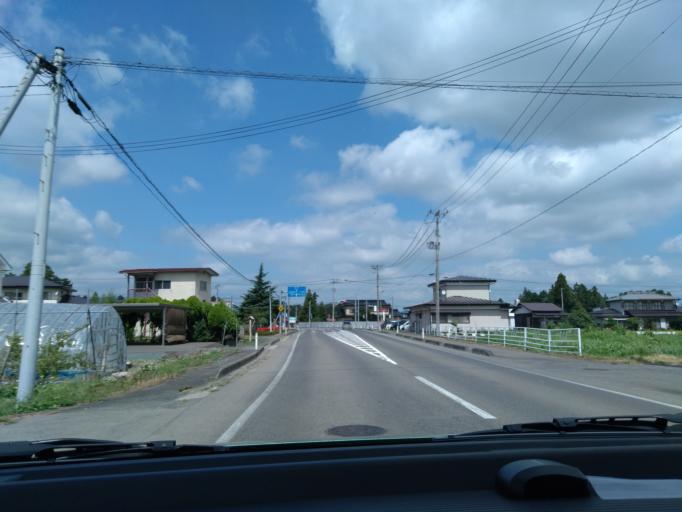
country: JP
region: Iwate
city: Hanamaki
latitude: 39.4431
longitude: 141.0987
